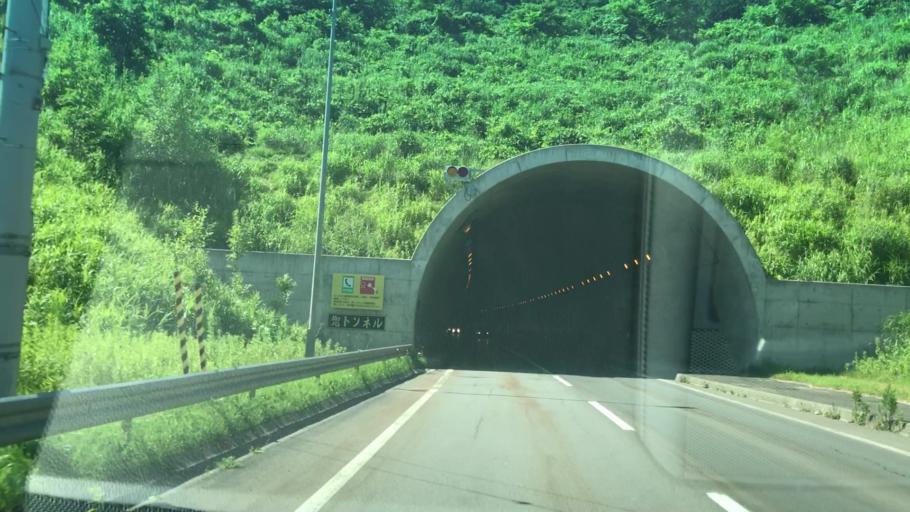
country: JP
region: Hokkaido
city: Iwanai
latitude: 43.0827
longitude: 140.4758
